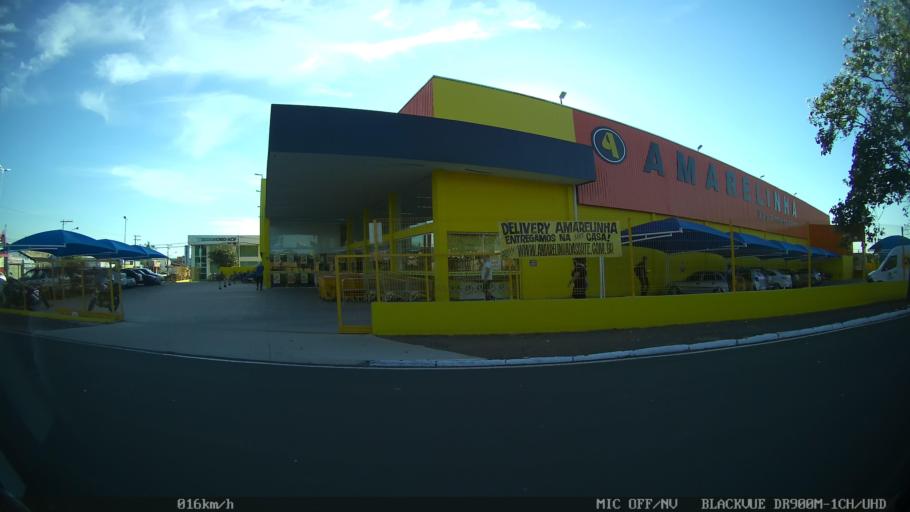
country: BR
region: Sao Paulo
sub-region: Franca
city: Franca
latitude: -20.5259
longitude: -47.3772
